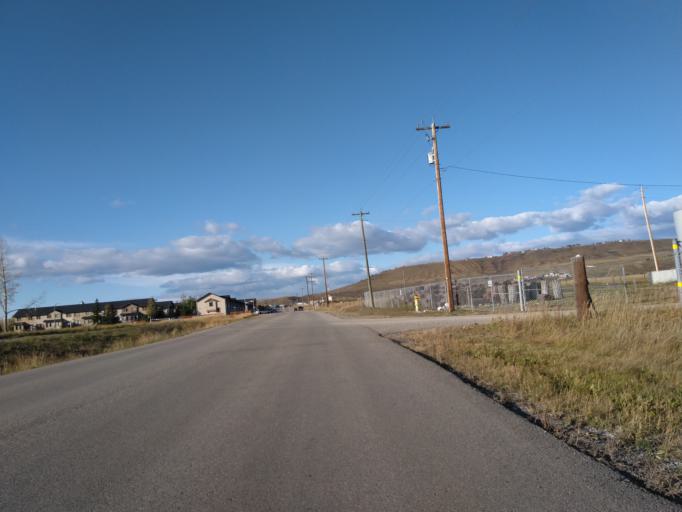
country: CA
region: Alberta
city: Cochrane
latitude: 51.1753
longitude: -114.4668
